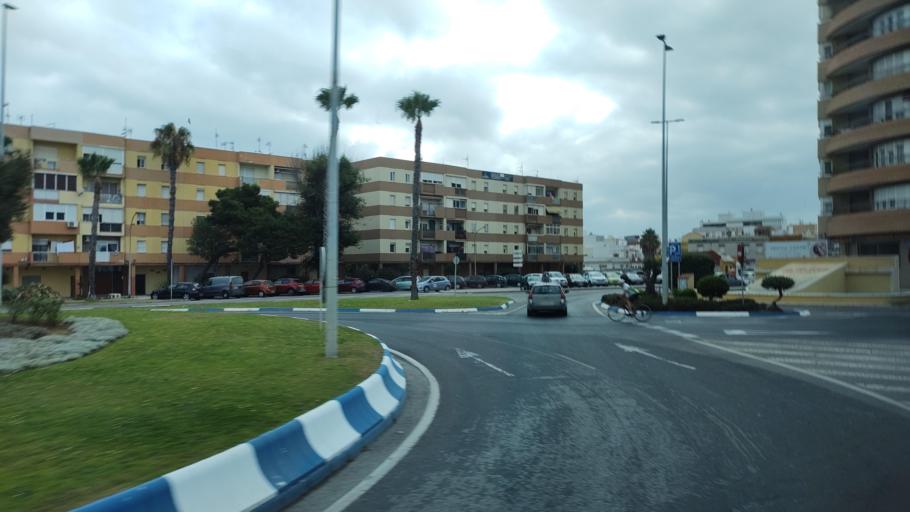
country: ES
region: Andalusia
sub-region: Provincia de Cadiz
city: La Linea de la Concepcion
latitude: 36.1622
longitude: -5.3571
